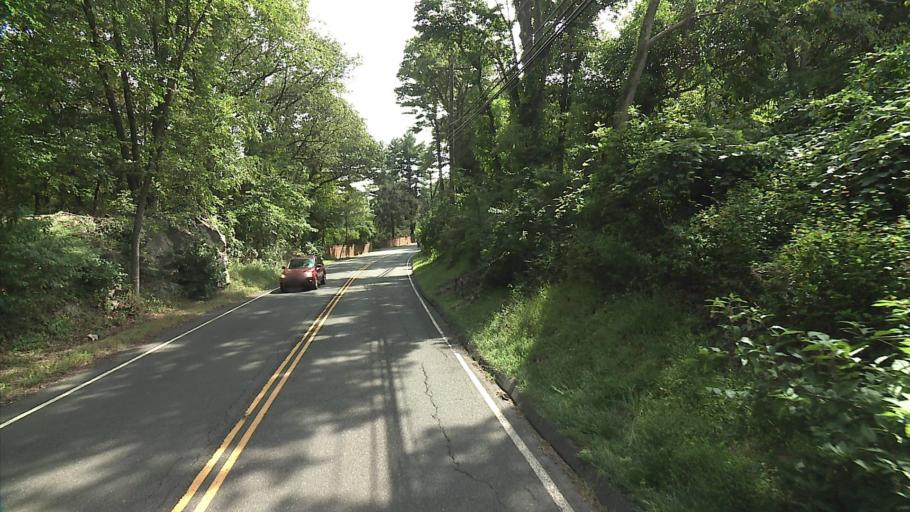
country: US
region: Connecticut
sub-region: Fairfield County
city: North Stamford
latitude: 41.1666
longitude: -73.5616
